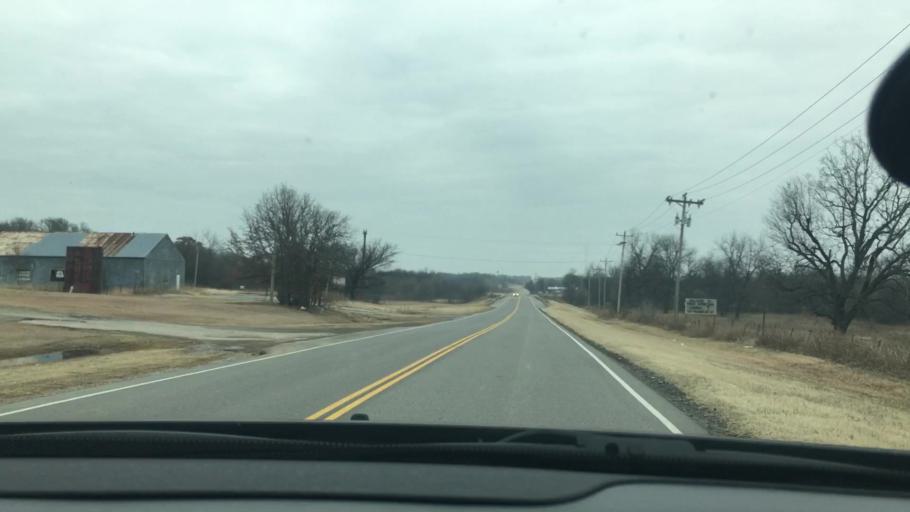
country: US
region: Oklahoma
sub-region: Carter County
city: Healdton
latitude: 34.2502
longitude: -97.4923
